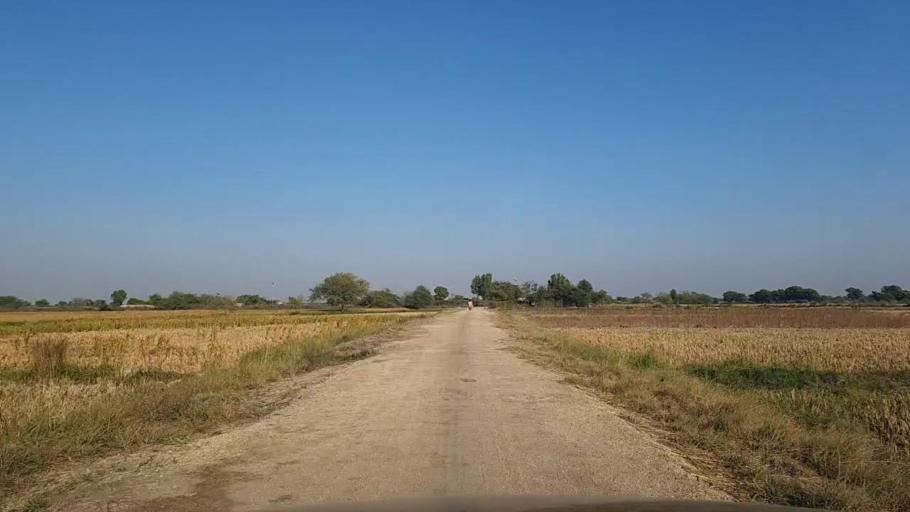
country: PK
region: Sindh
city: Mirpur Batoro
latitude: 24.6842
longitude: 68.3633
